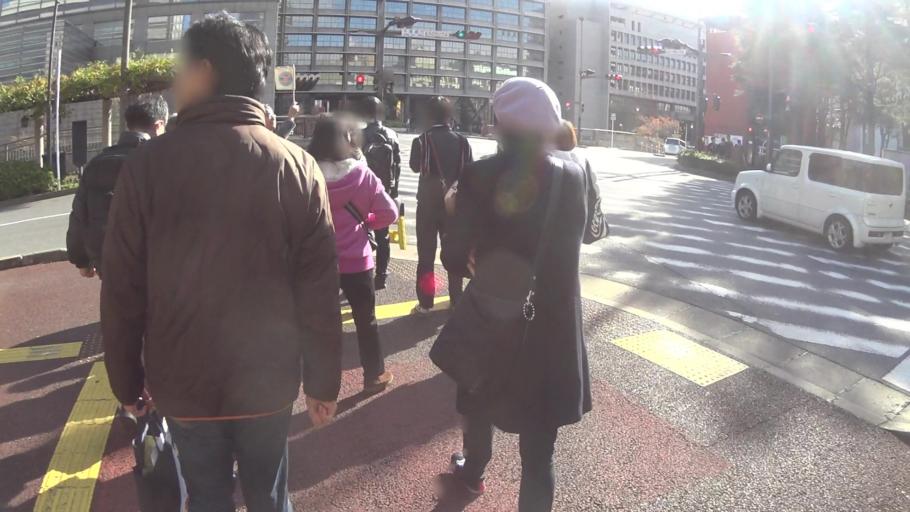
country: JP
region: Chiba
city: Chiba
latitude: 35.6056
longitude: 140.1229
